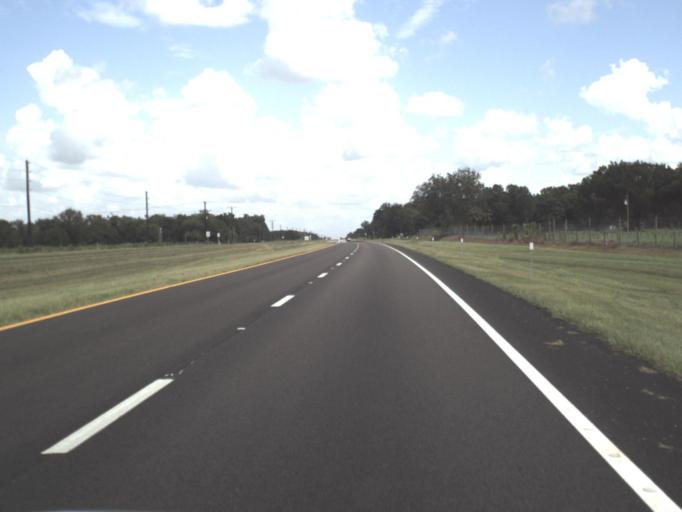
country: US
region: Florida
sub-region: Hardee County
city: Zolfo Springs
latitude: 27.4089
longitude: -81.7952
